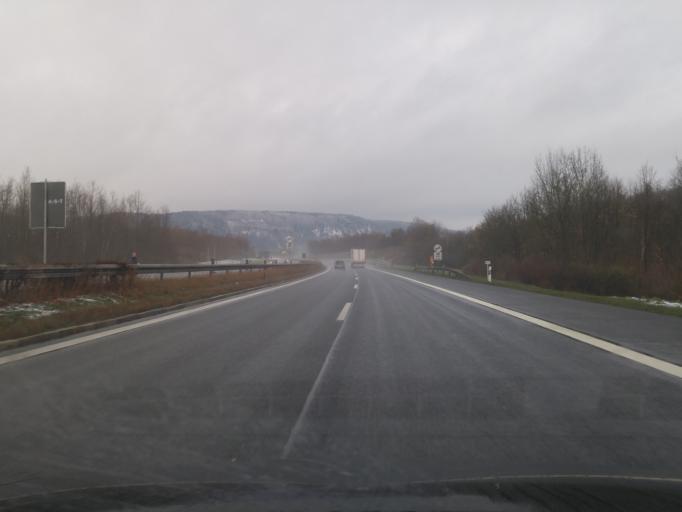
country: DE
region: Bavaria
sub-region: Regierungsbezirk Unterfranken
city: Elfershausen
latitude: 50.1250
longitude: 9.9588
